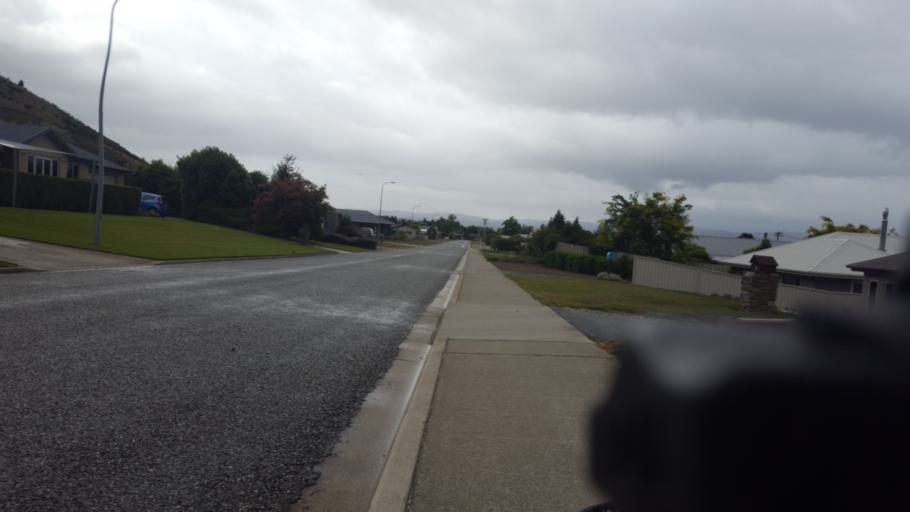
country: NZ
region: Otago
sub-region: Queenstown-Lakes District
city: Wanaka
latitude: -45.1882
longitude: 169.3265
